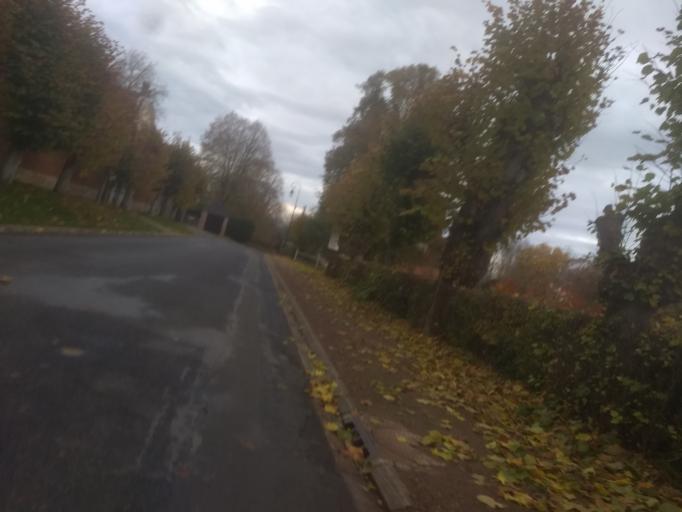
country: FR
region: Nord-Pas-de-Calais
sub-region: Departement du Pas-de-Calais
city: Riviere
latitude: 50.2348
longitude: 2.6876
